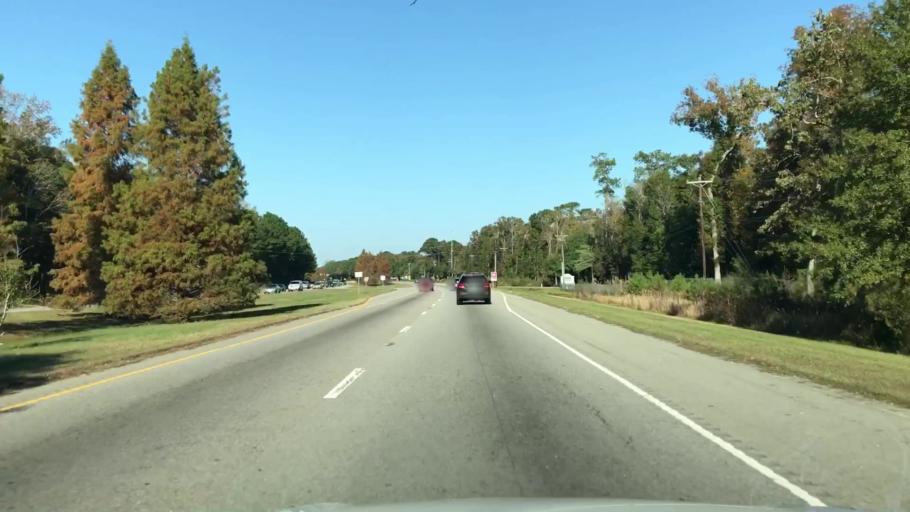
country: US
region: South Carolina
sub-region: Charleston County
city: Shell Point
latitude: 32.8160
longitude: -80.0621
